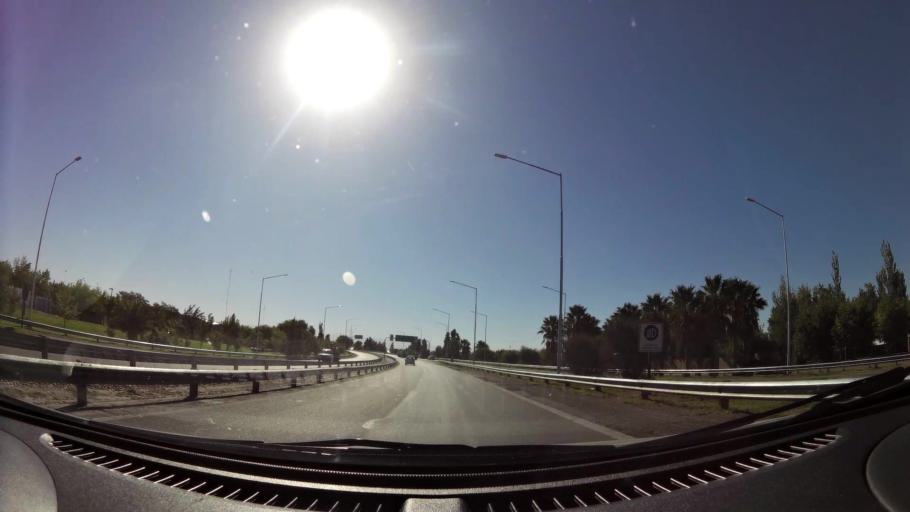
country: AR
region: San Juan
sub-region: Departamento de Santa Lucia
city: Santa Lucia
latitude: -31.5184
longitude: -68.5062
